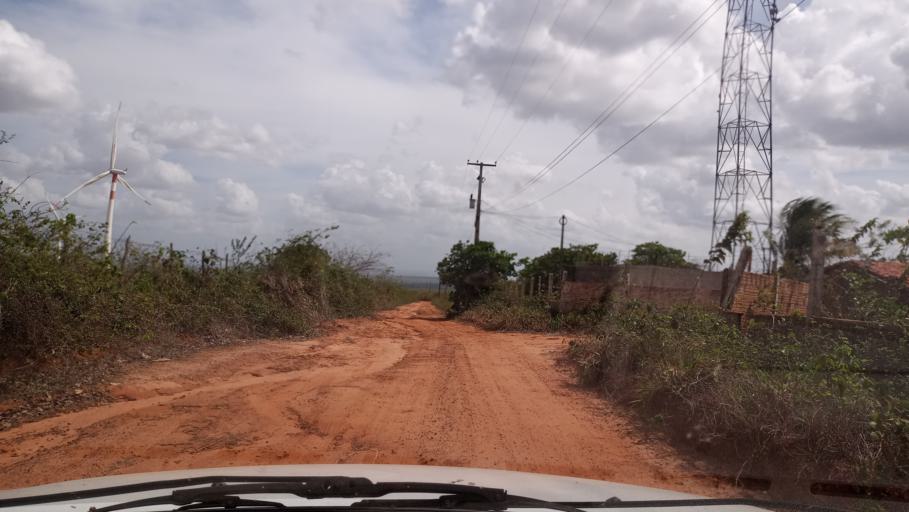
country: BR
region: Rio Grande do Norte
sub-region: Joao Camara
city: Joao Camara
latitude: -5.4180
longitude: -35.8565
